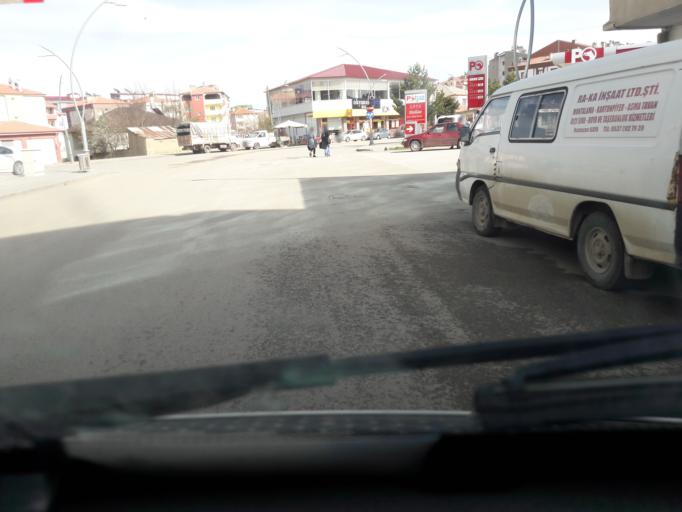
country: TR
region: Gumushane
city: Kelkit
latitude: 40.1343
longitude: 39.4352
